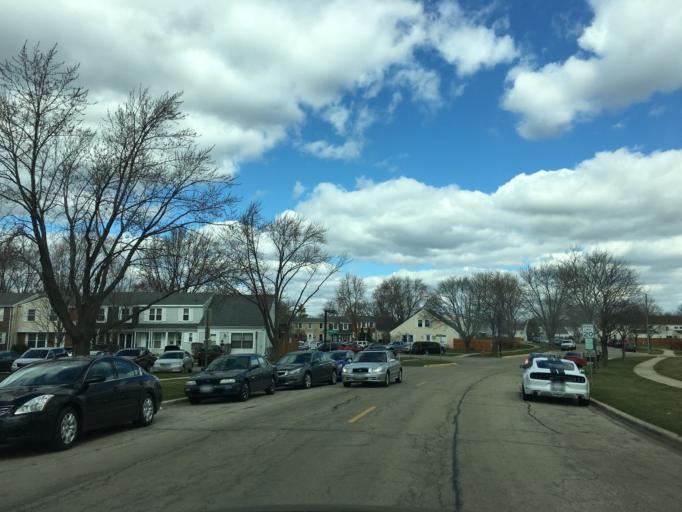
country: US
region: Illinois
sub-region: DuPage County
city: Hanover Park
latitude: 42.0079
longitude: -88.1300
